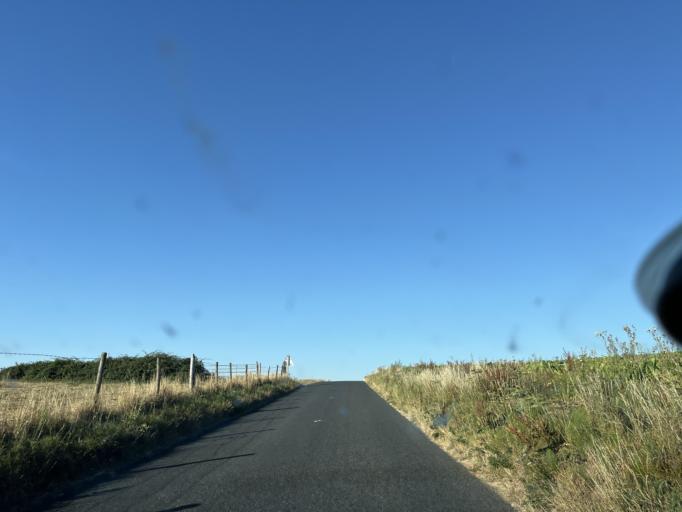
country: FR
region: Haute-Normandie
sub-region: Departement de la Seine-Maritime
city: Lillebonne
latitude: 49.5516
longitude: 0.5689
